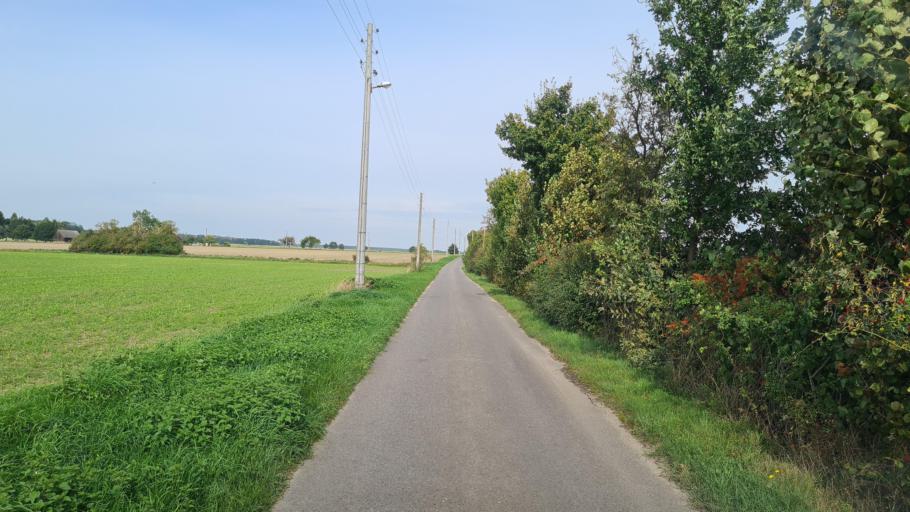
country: DE
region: Brandenburg
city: Sonnewalde
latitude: 51.7161
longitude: 13.6260
